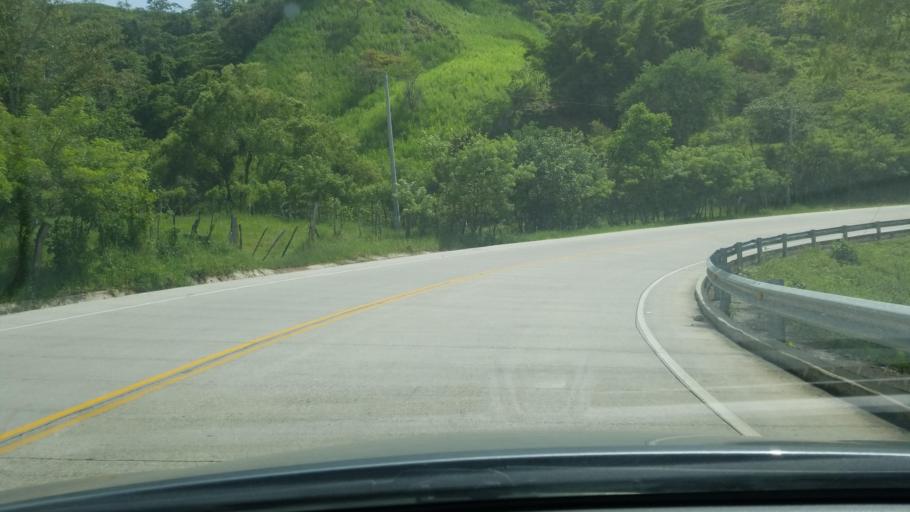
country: HN
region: Copan
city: San Jeronimo
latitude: 14.9577
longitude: -88.9071
